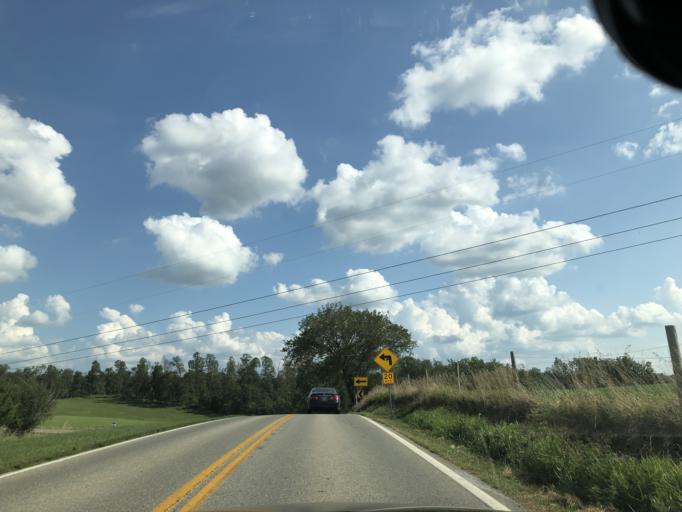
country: US
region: Maryland
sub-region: Frederick County
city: Linganore
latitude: 39.4087
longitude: -77.2045
